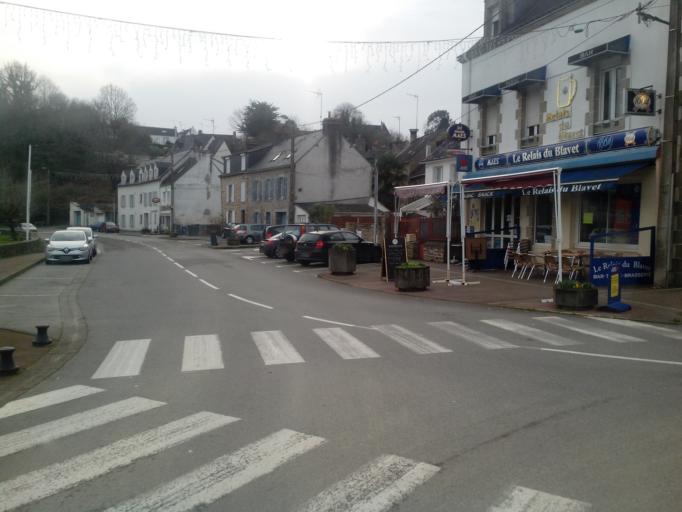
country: FR
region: Brittany
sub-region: Departement du Morbihan
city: Hennebont
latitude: 47.8060
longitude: -3.2833
